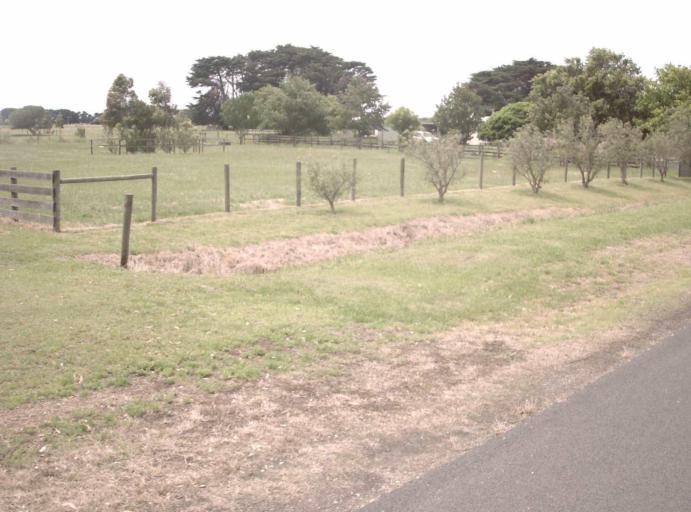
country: AU
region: Victoria
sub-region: Wellington
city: Sale
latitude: -38.0546
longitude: 147.0249
